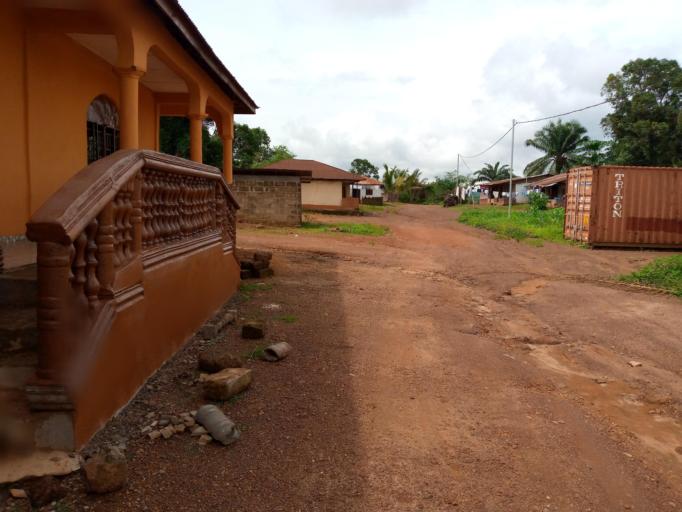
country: SL
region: Southern Province
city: Mogbwemo
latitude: 7.7606
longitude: -12.3086
